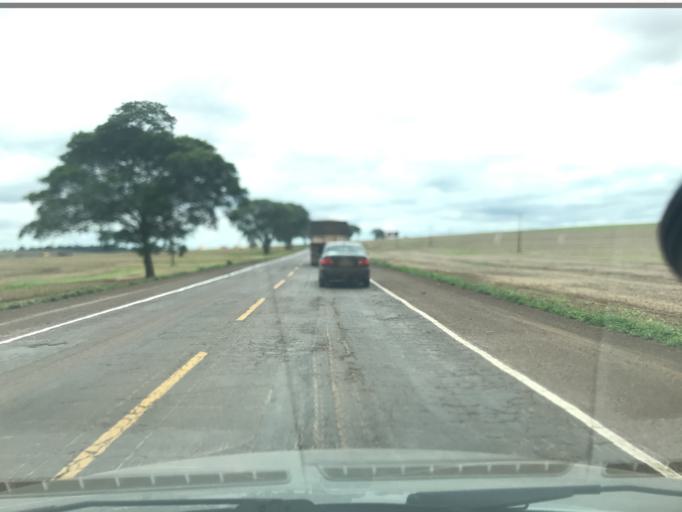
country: BR
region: Parana
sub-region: Terra Boa
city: Terra Boa
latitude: -23.6080
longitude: -52.4184
